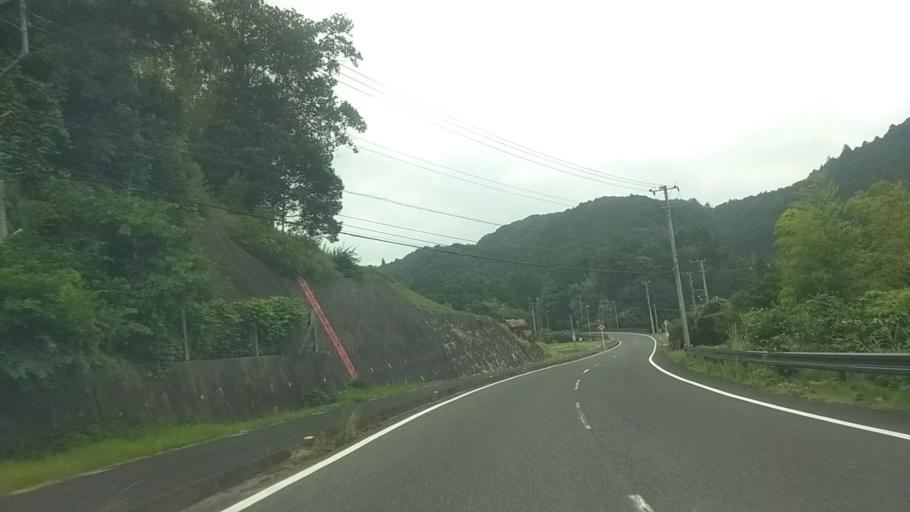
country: JP
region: Chiba
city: Kawaguchi
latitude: 35.2294
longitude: 140.1146
